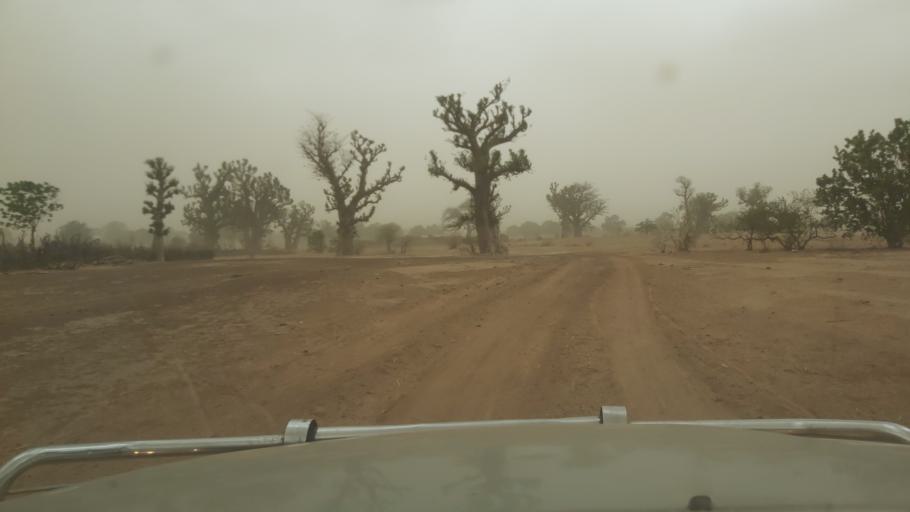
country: ML
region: Koulikoro
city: Banamba
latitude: 13.3759
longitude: -7.2030
